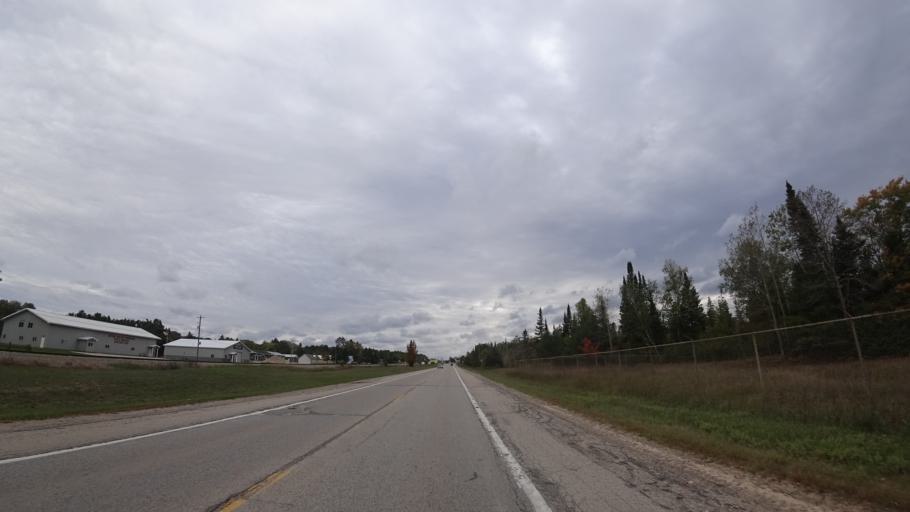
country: US
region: Michigan
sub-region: Charlevoix County
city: Boyne City
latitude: 45.1736
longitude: -84.9144
